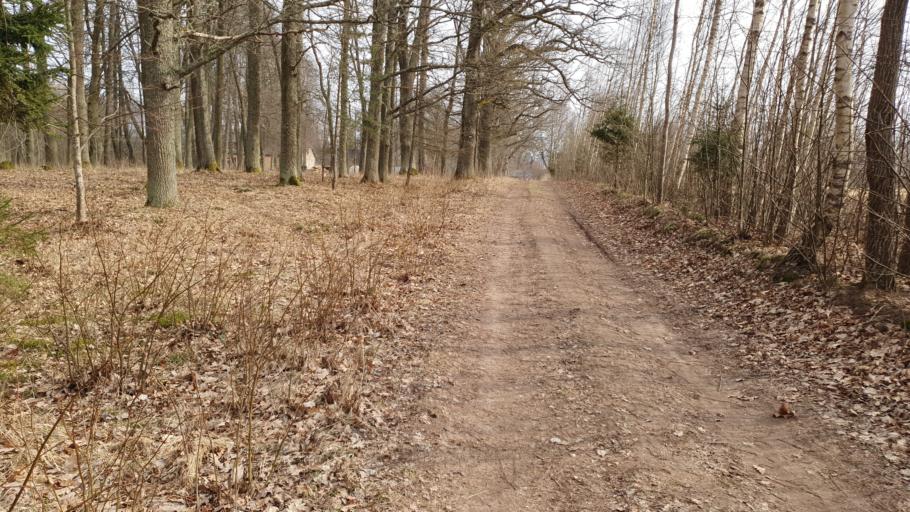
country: LV
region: Beverina
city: Murmuiza
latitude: 57.5496
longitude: 25.5277
